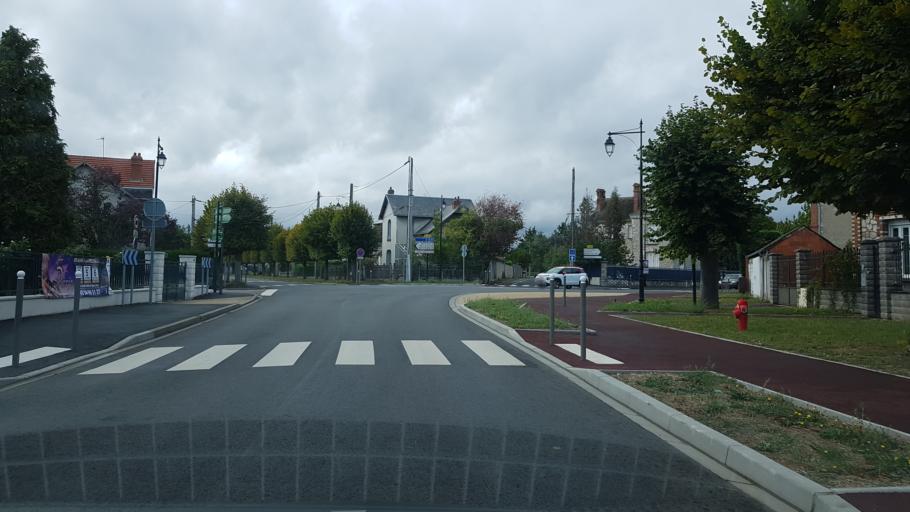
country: FR
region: Centre
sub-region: Departement du Loiret
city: Beaune-la-Rolande
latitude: 48.0720
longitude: 2.4278
